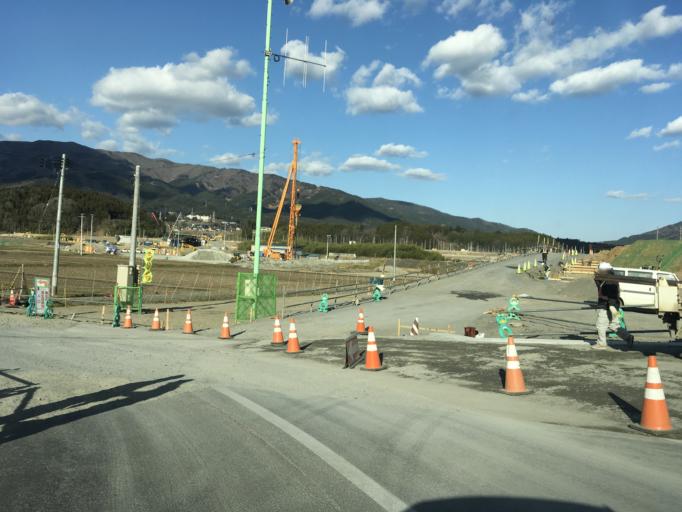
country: JP
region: Iwate
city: Ofunato
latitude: 39.0162
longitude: 141.6147
